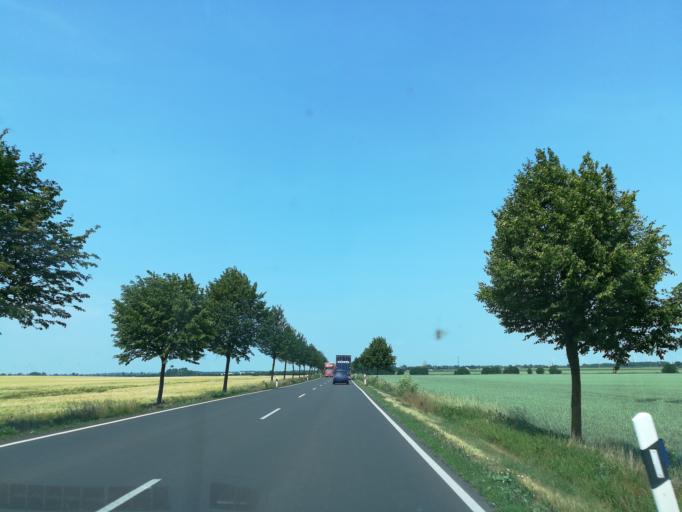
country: DE
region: Saxony-Anhalt
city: Schneidlingen
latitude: 51.9155
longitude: 11.4259
